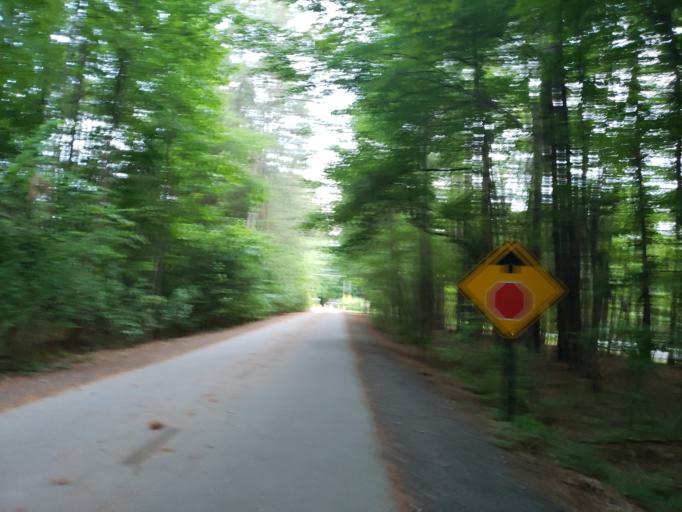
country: US
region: North Carolina
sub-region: Durham County
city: Durham
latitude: 35.9161
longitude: -78.9339
